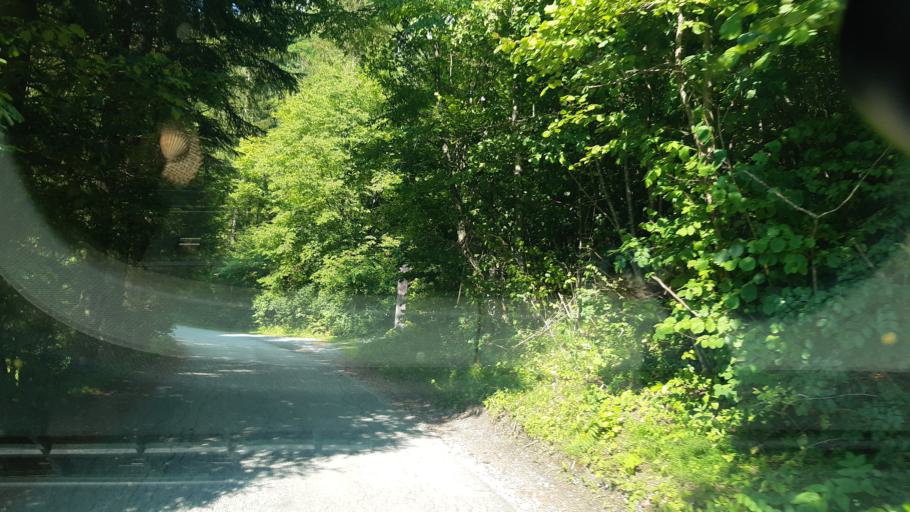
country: SI
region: Radovljica
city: Radovljica
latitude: 46.3811
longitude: 14.2177
